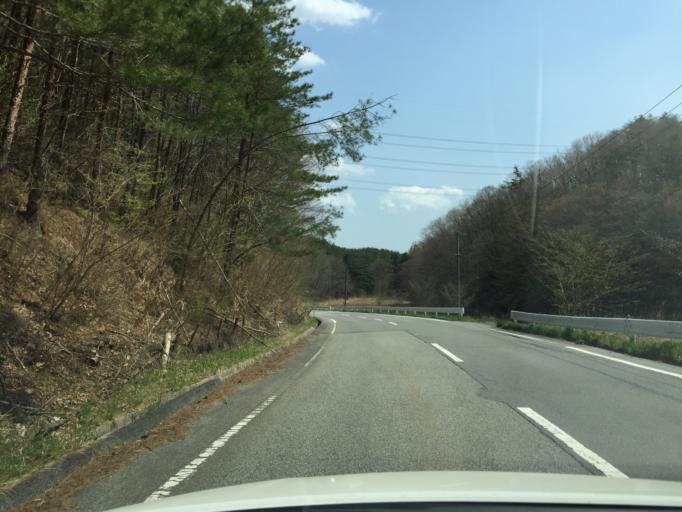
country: JP
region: Fukushima
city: Namie
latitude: 37.3777
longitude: 140.8007
